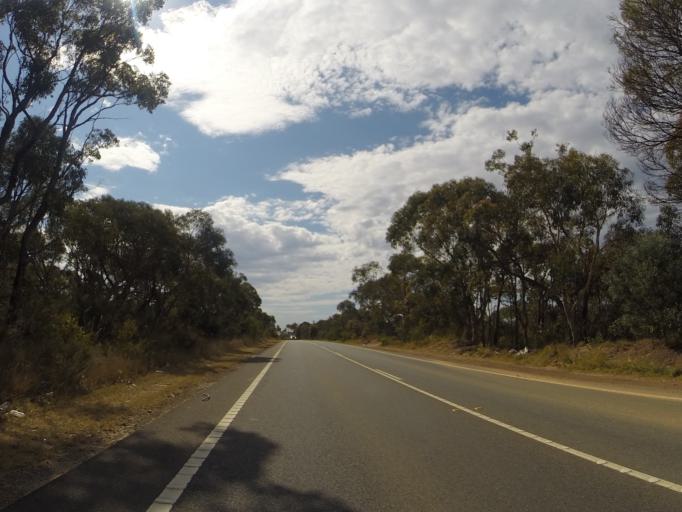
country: AU
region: New South Wales
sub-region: Sutherland Shire
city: Menai
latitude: -34.0030
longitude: 150.9939
